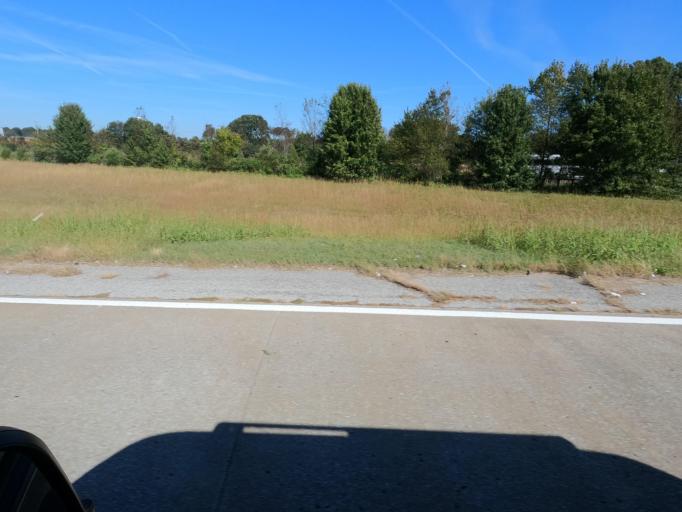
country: US
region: Tennessee
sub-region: Crockett County
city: Alamo
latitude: 35.7750
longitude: -89.1271
